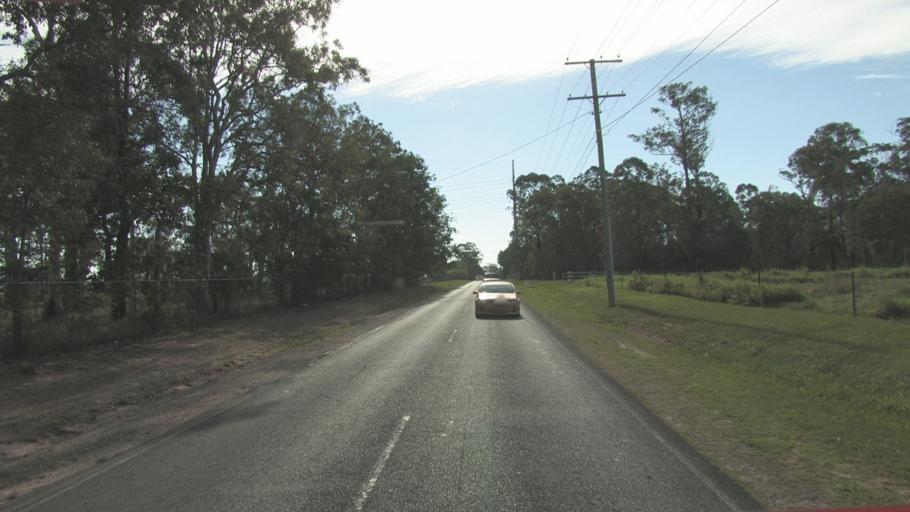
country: AU
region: Queensland
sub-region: Logan
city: Logan Reserve
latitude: -27.7053
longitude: 153.0678
